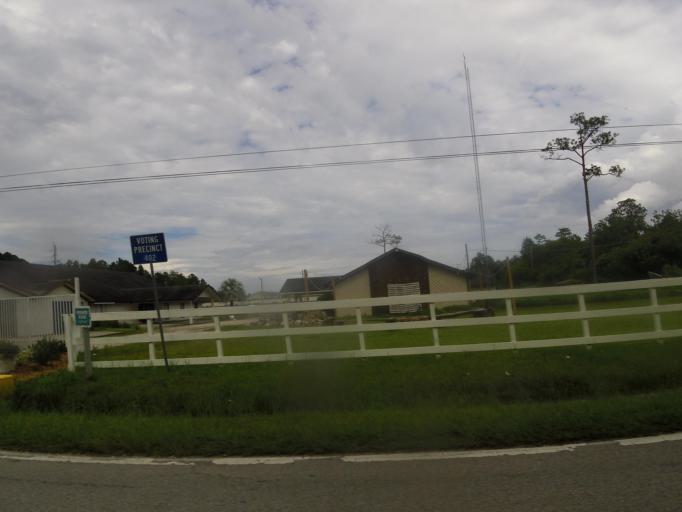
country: US
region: Florida
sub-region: Duval County
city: Jacksonville
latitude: 30.3067
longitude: -81.5313
